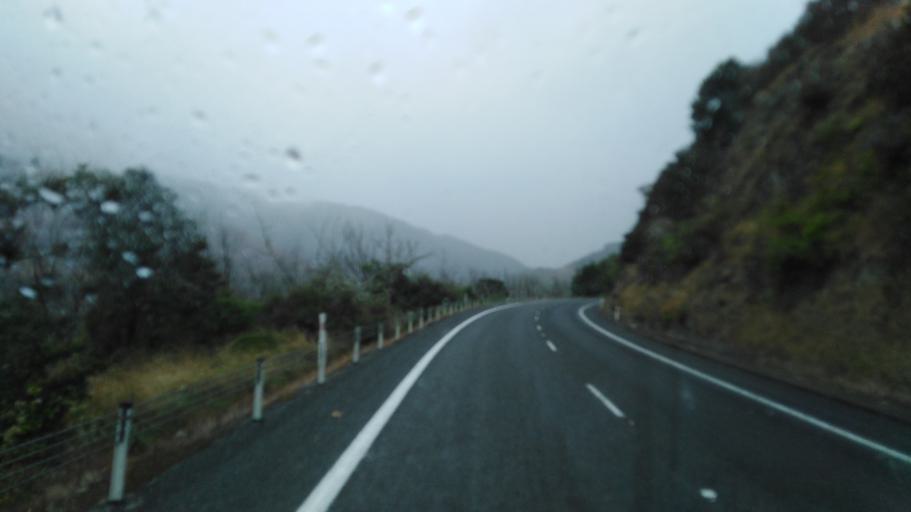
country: NZ
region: Marlborough
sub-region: Marlborough District
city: Blenheim
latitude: -41.4055
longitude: 173.9586
